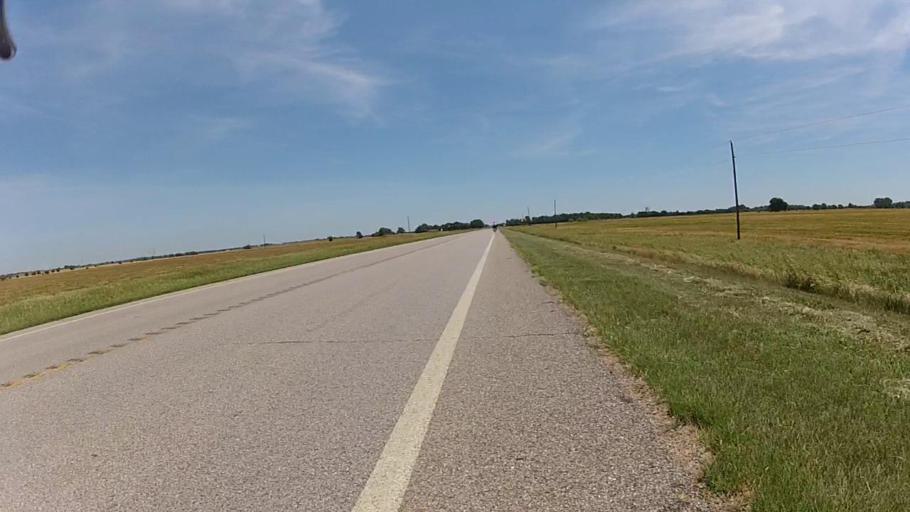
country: US
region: Kansas
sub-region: Barber County
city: Medicine Lodge
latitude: 37.2533
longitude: -98.4434
